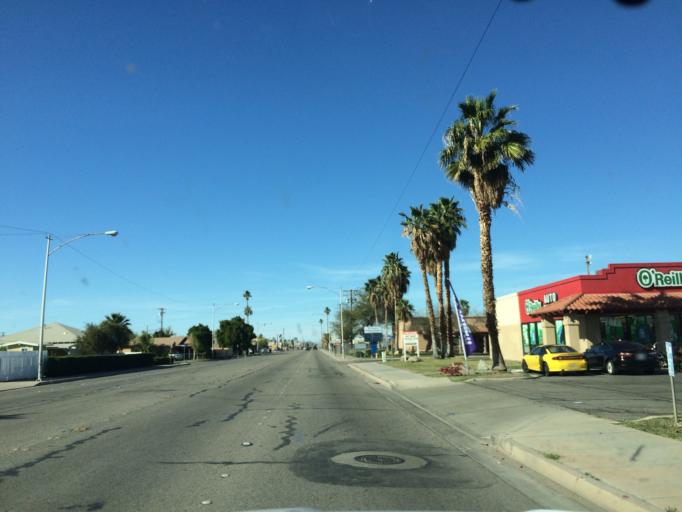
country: US
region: California
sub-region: Imperial County
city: El Centro
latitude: 32.7823
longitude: -115.5524
